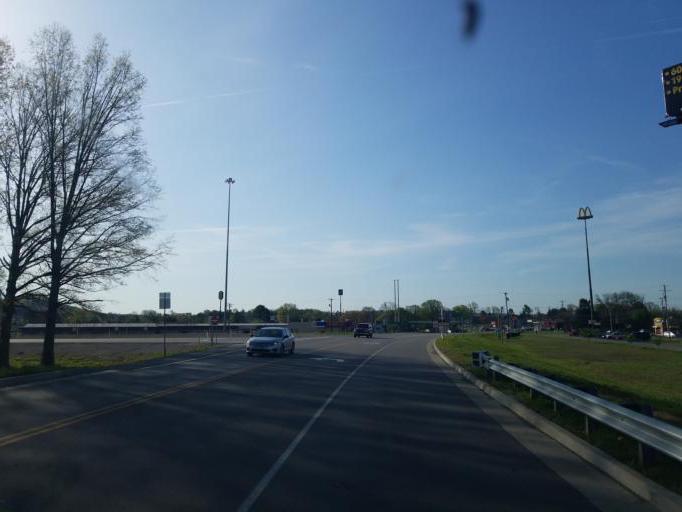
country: US
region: Kentucky
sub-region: Hart County
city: Munfordville
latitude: 37.2911
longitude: -85.9033
